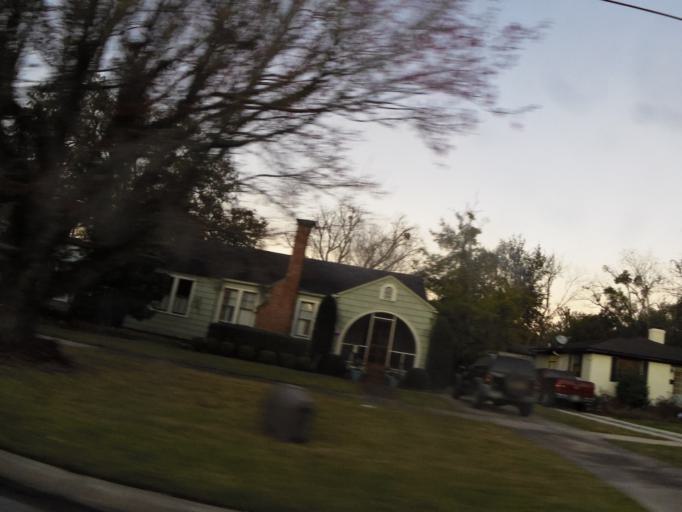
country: US
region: Florida
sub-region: Duval County
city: Jacksonville
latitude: 30.3008
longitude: -81.7047
